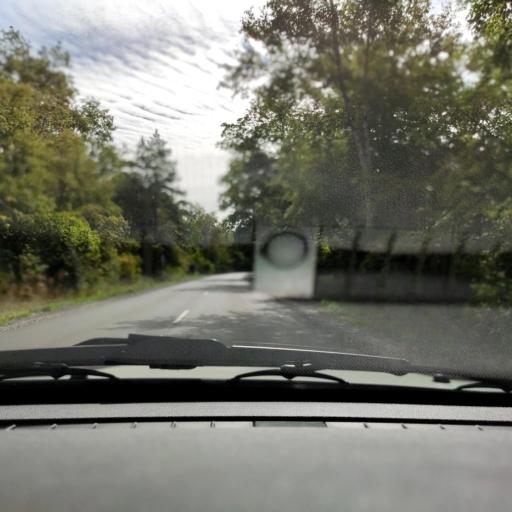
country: RU
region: Voronezj
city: Krasnolesnyy
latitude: 51.8738
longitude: 39.6541
